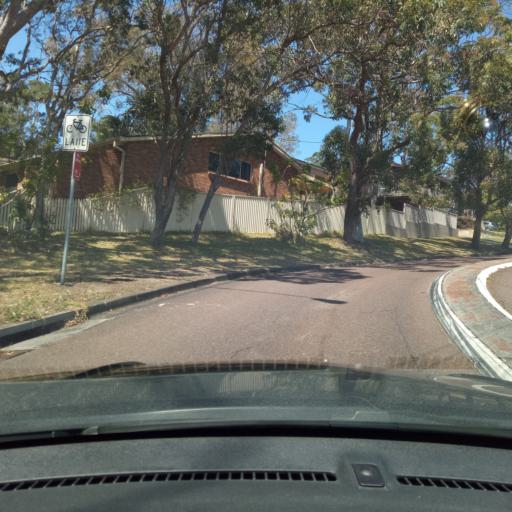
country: AU
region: New South Wales
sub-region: Wyong Shire
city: Bateau Bay
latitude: -33.3802
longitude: 151.4638
